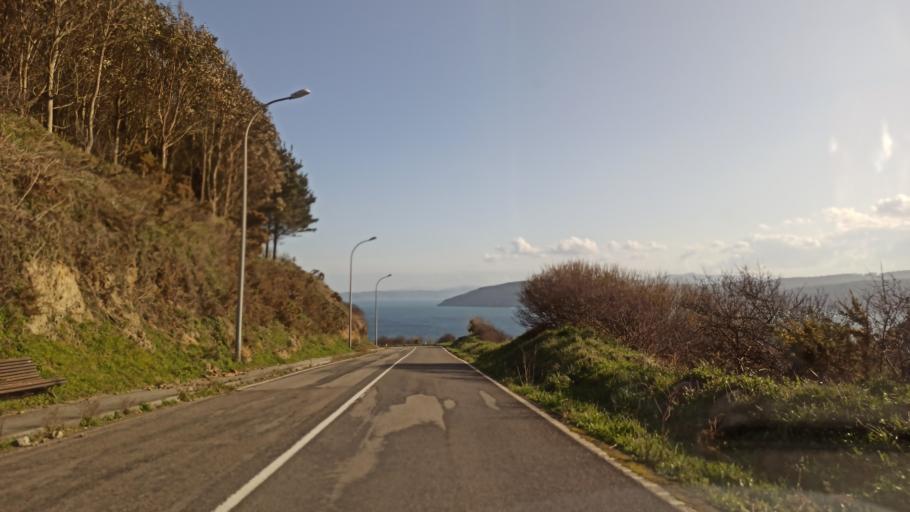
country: ES
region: Galicia
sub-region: Provincia da Coruna
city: Manon
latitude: 43.7727
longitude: -7.6806
